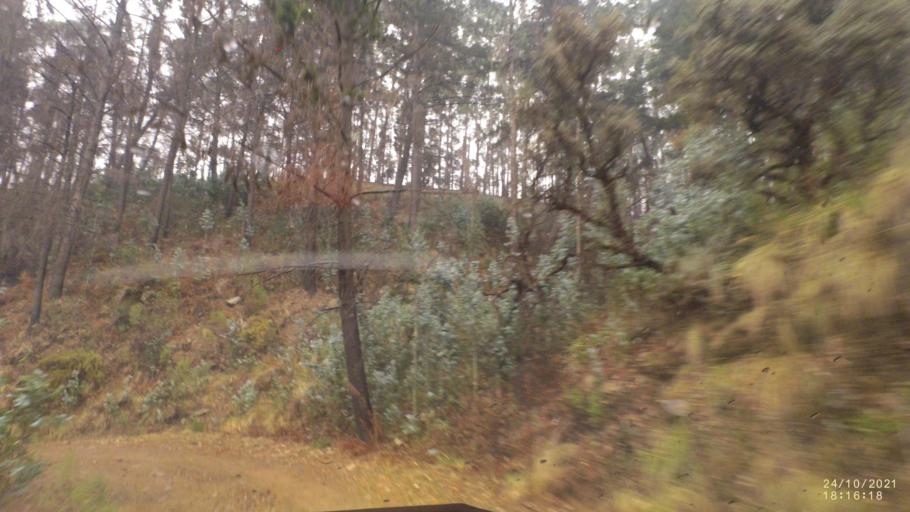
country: BO
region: Cochabamba
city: Cochabamba
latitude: -17.3314
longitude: -66.1373
